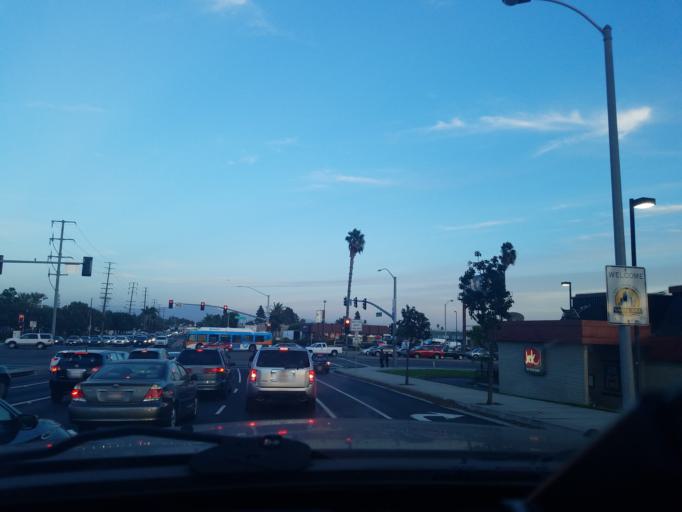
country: US
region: California
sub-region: Orange County
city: Fountain Valley
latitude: 33.7138
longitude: -117.9205
